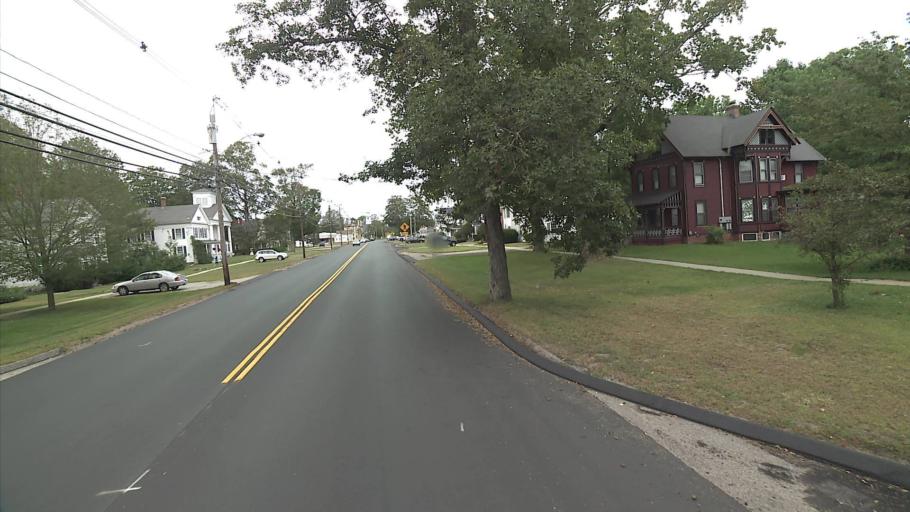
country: US
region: Connecticut
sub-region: New London County
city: Colchester
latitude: 41.5707
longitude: -72.3305
